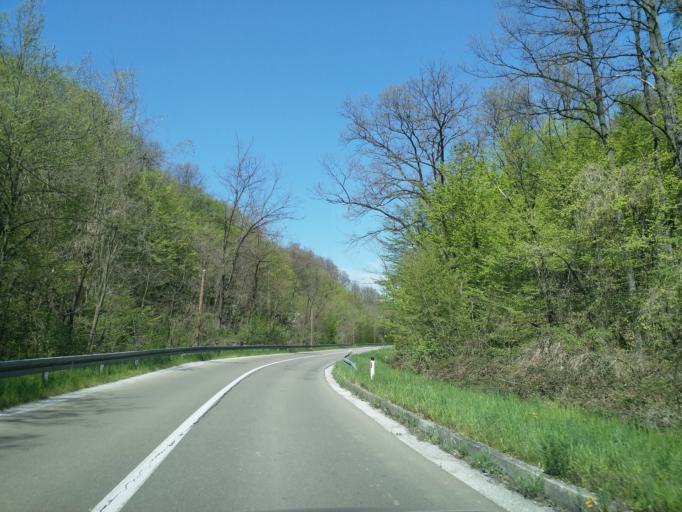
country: RS
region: Central Serbia
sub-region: Belgrade
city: Lazarevac
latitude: 44.3573
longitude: 20.3514
